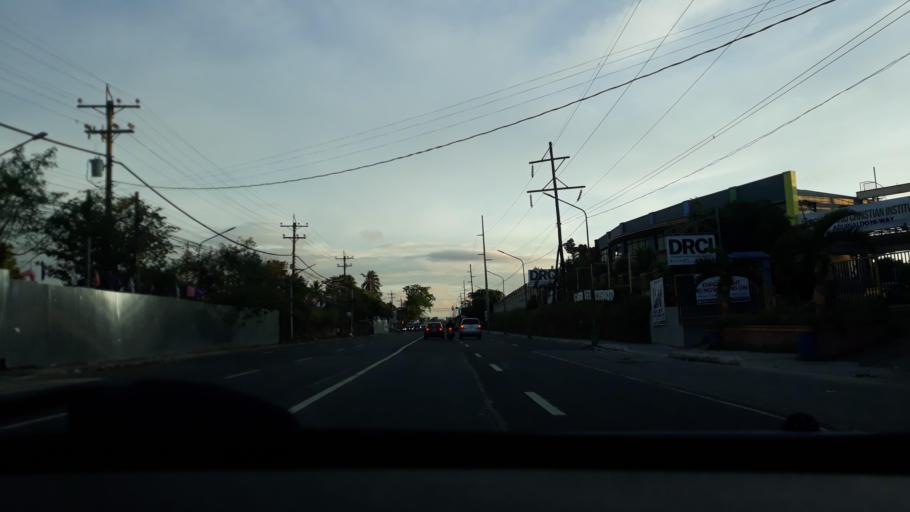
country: PH
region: Calabarzon
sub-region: Province of Cavite
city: Silang
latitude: 14.2317
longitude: 120.9713
